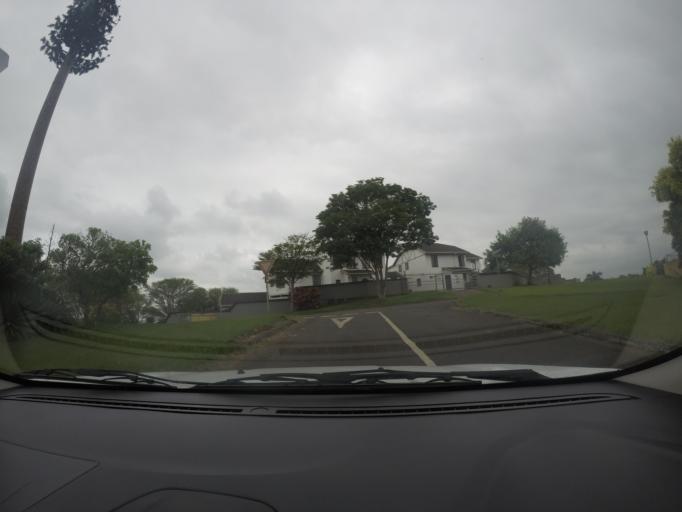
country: ZA
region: KwaZulu-Natal
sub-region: uThungulu District Municipality
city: Empangeni
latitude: -28.7591
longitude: 31.8884
